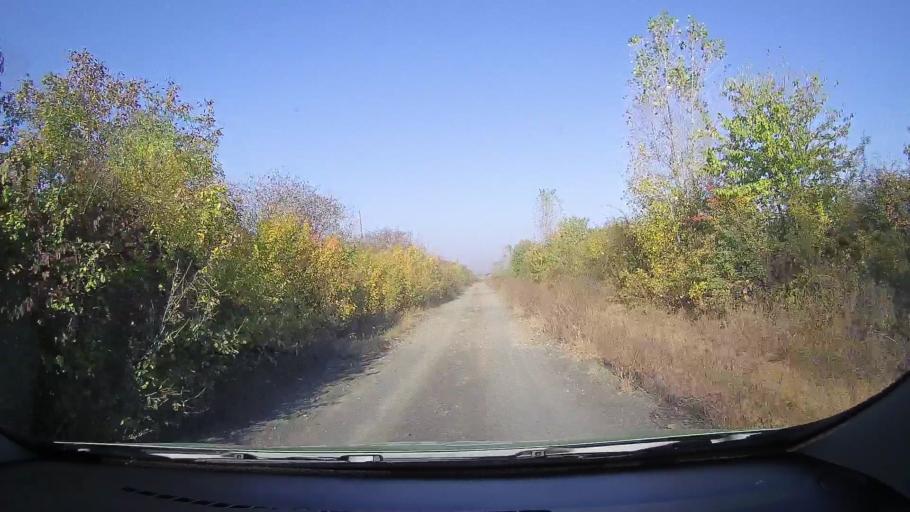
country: RO
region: Satu Mare
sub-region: Comuna Sauca
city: Sauca
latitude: 47.4753
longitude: 22.4787
